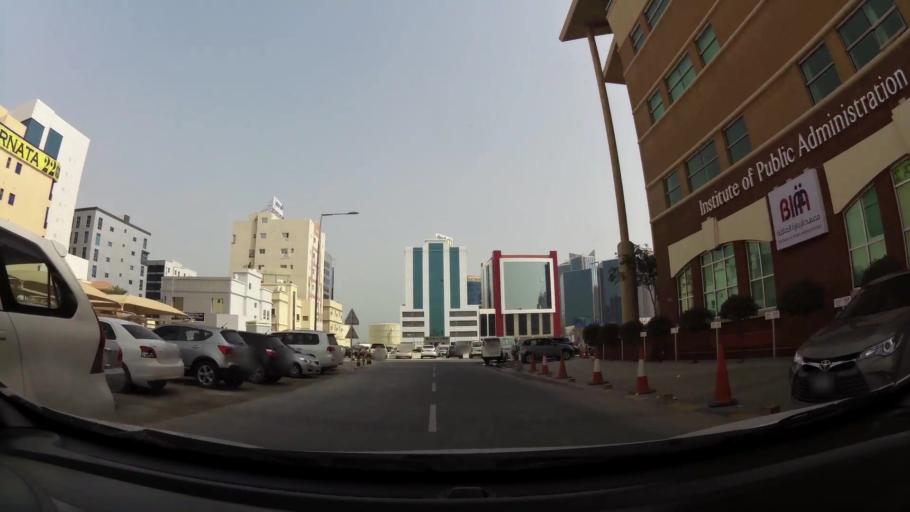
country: BH
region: Manama
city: Jidd Hafs
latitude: 26.2364
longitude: 50.5324
